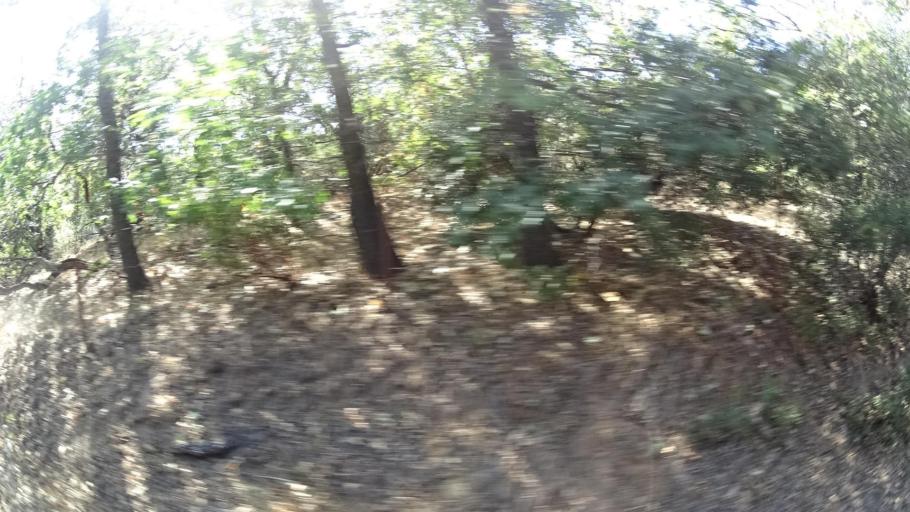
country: US
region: California
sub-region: San Diego County
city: Julian
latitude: 33.0748
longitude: -116.5856
